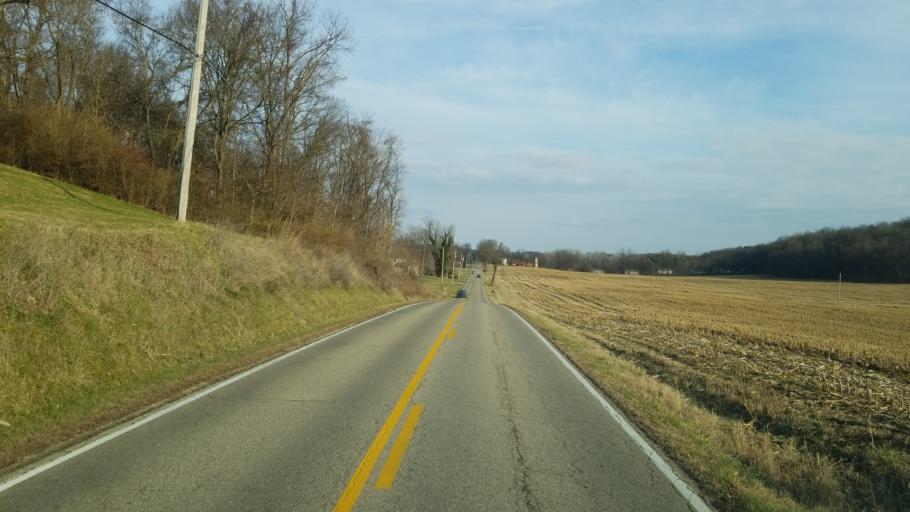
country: US
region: Ohio
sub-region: Ross County
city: Kingston
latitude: 39.4136
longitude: -82.9407
